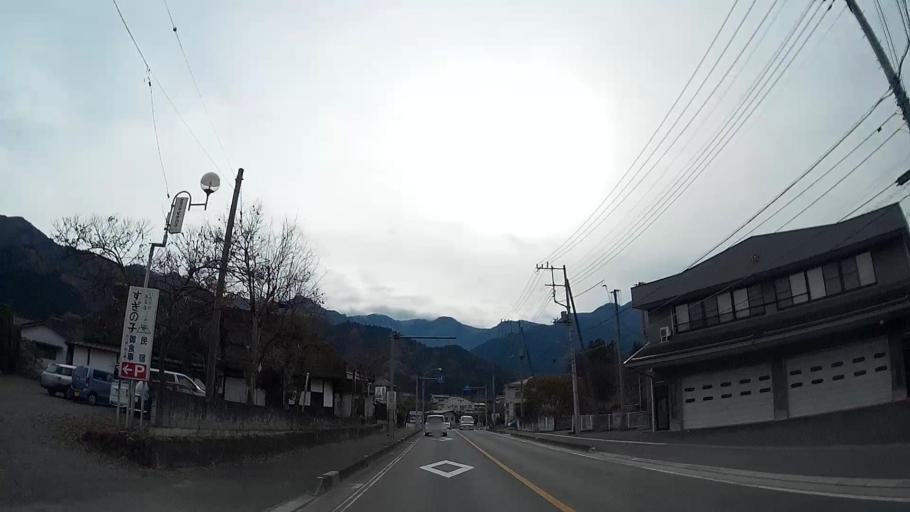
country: JP
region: Saitama
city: Chichibu
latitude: 35.9571
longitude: 139.0303
